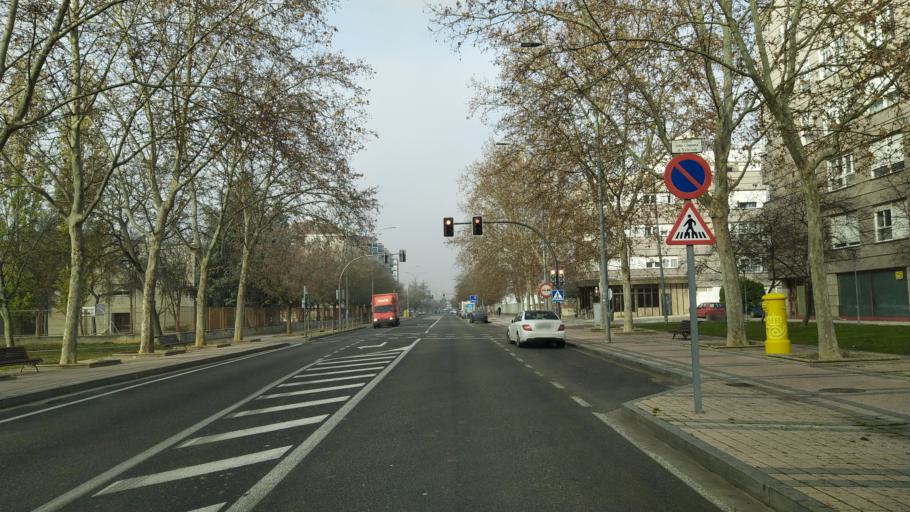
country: ES
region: Castille and Leon
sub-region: Provincia de Palencia
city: Palencia
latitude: 41.9954
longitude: -4.5179
